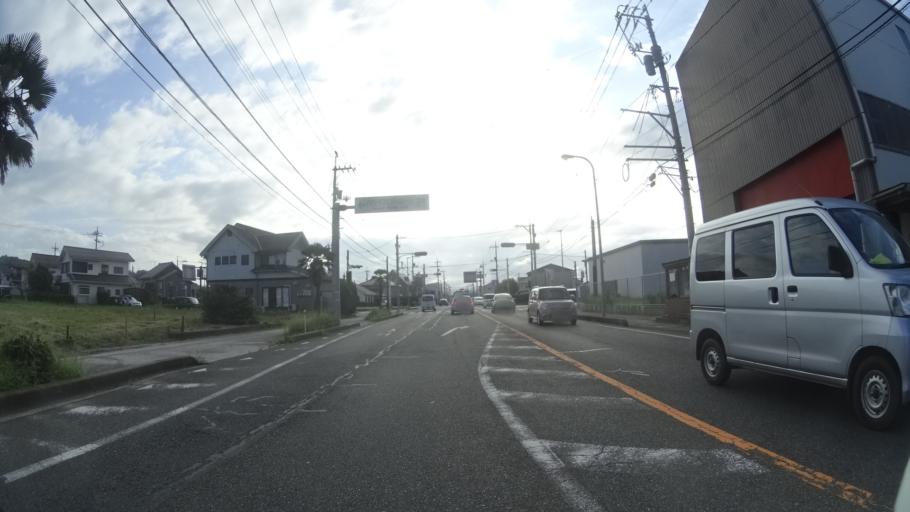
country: JP
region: Tottori
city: Kurayoshi
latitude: 35.4890
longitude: 133.8649
